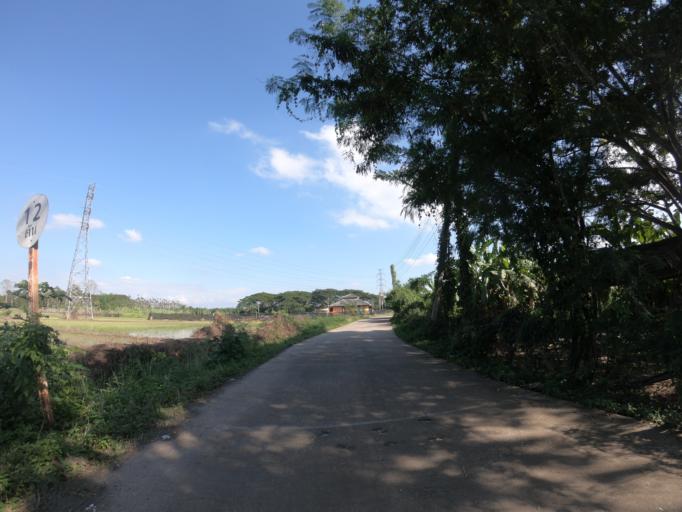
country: TH
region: Chiang Mai
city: Saraphi
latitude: 18.7142
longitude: 99.0087
